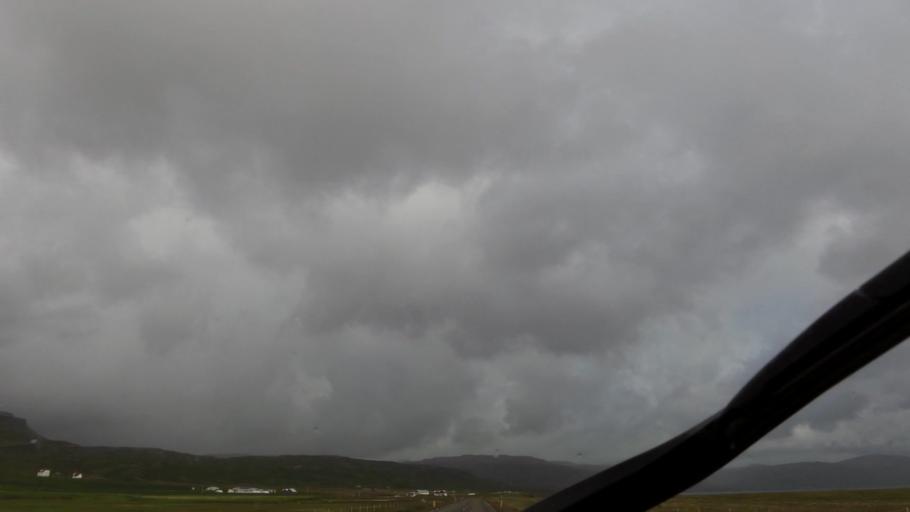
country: IS
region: Westfjords
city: Isafjoerdur
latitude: 65.5208
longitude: -23.1869
